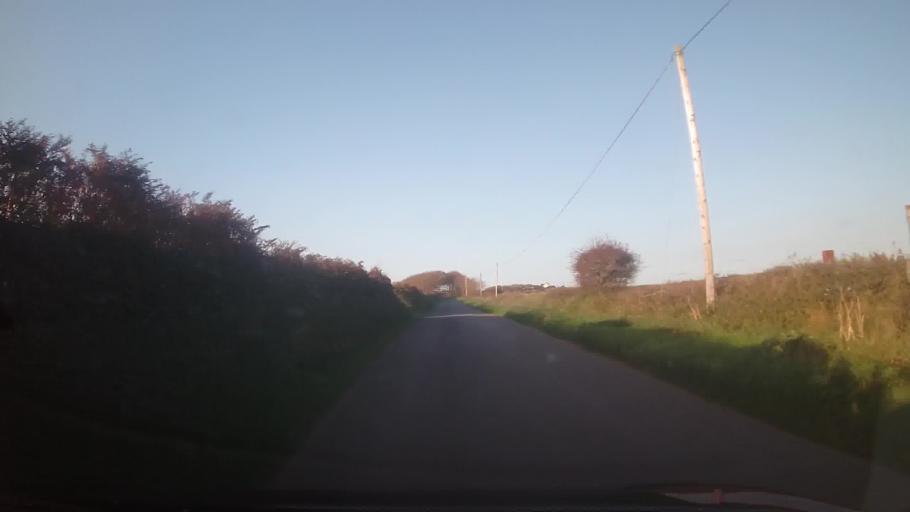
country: GB
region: Wales
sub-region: Pembrokeshire
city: Saint David's
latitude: 51.9121
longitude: -5.2408
